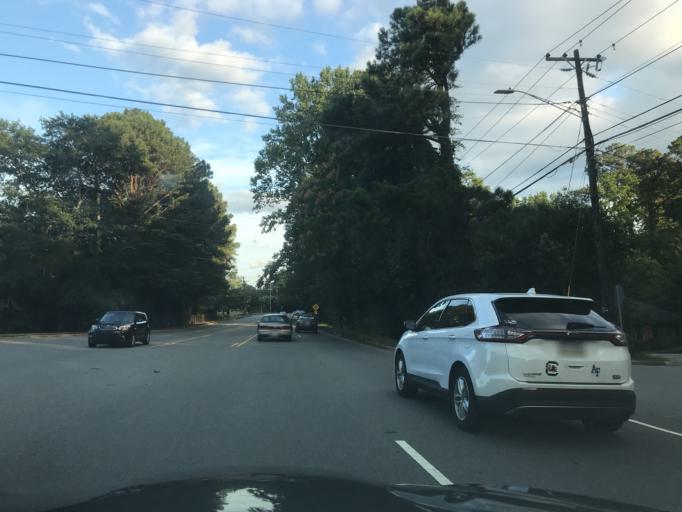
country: US
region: North Carolina
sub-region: Wake County
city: West Raleigh
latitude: 35.8320
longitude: -78.6367
